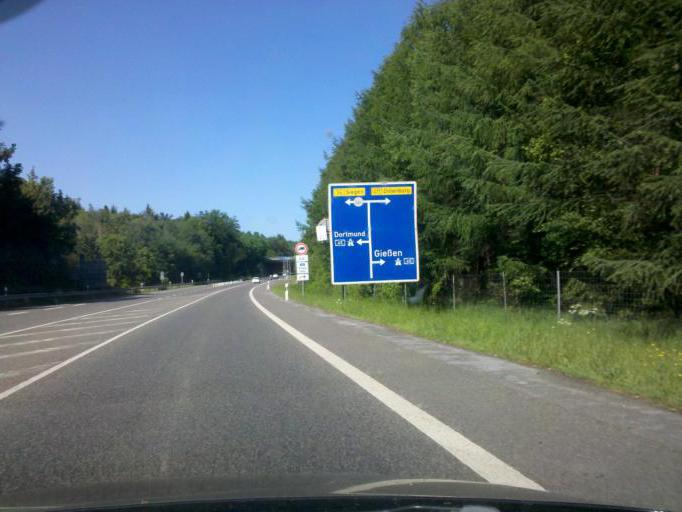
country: DE
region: Hesse
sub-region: Regierungsbezirk Giessen
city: Haiger
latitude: 50.7606
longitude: 8.1504
